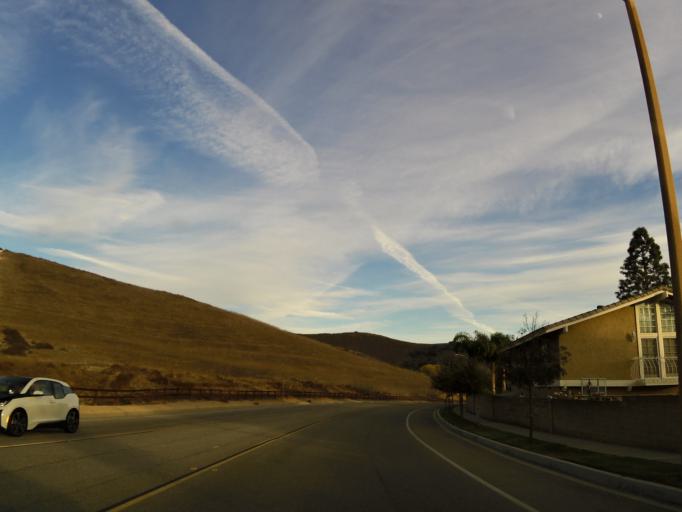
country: US
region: California
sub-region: Ventura County
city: Thousand Oaks
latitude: 34.1729
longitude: -118.8268
